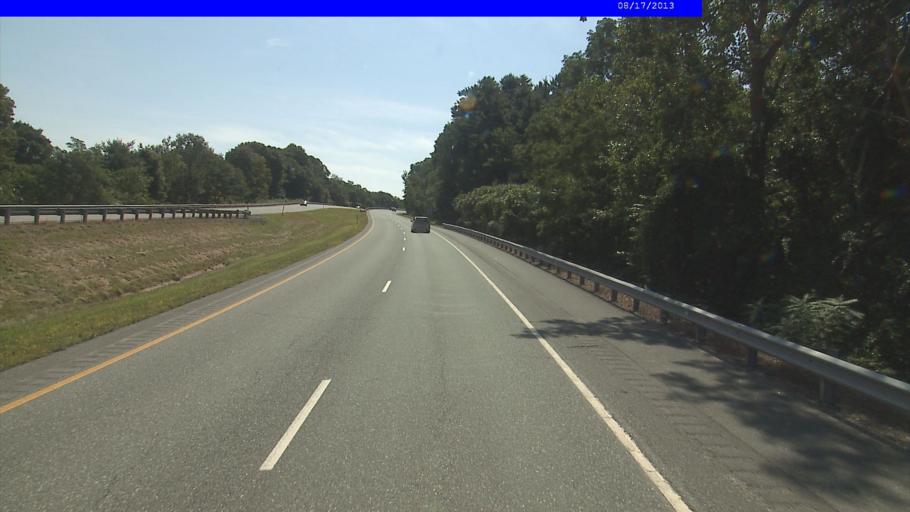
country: US
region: Vermont
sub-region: Windham County
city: Brattleboro
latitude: 42.8476
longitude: -72.5774
